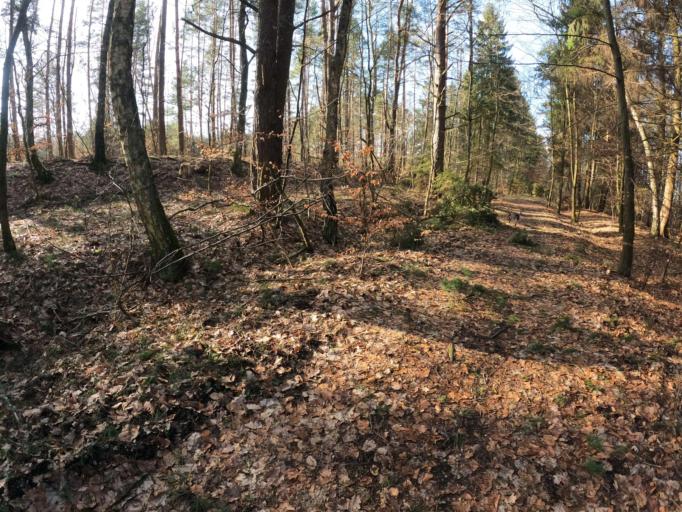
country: PL
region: West Pomeranian Voivodeship
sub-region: Powiat koszalinski
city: Polanow
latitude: 54.1126
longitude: 16.6969
